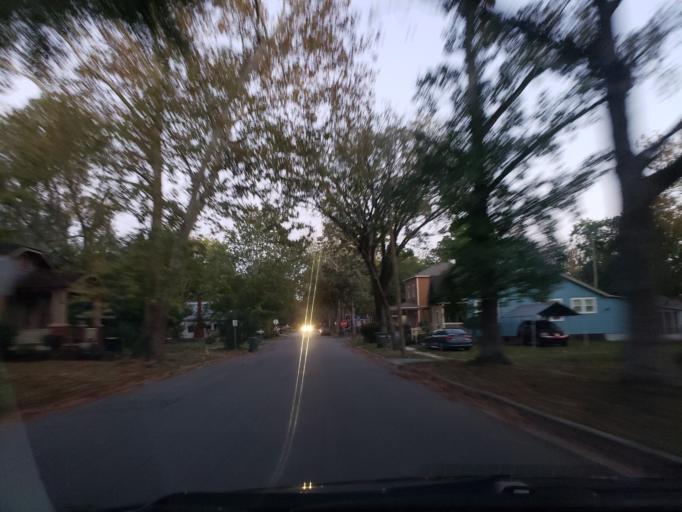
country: US
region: Georgia
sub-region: Chatham County
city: Savannah
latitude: 32.0561
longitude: -81.0774
